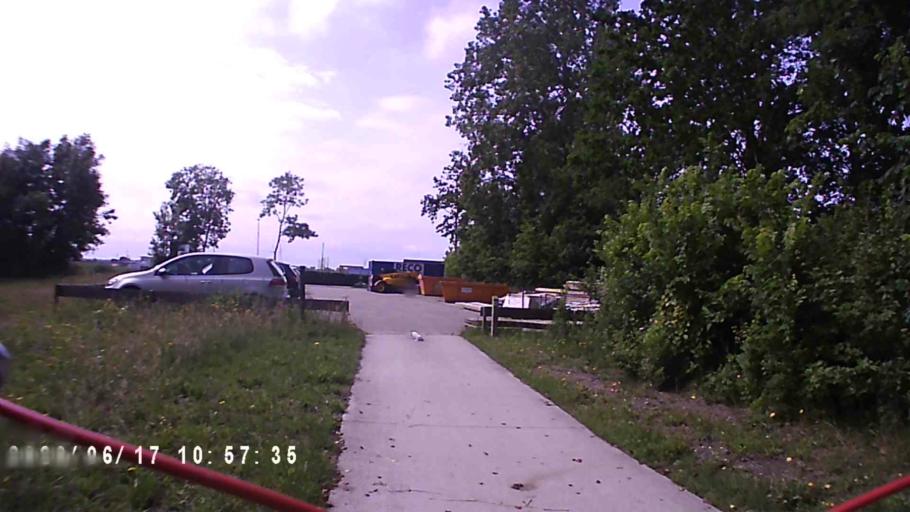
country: NL
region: Friesland
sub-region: Gemeente Dongeradeel
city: Anjum
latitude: 53.4057
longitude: 6.2081
